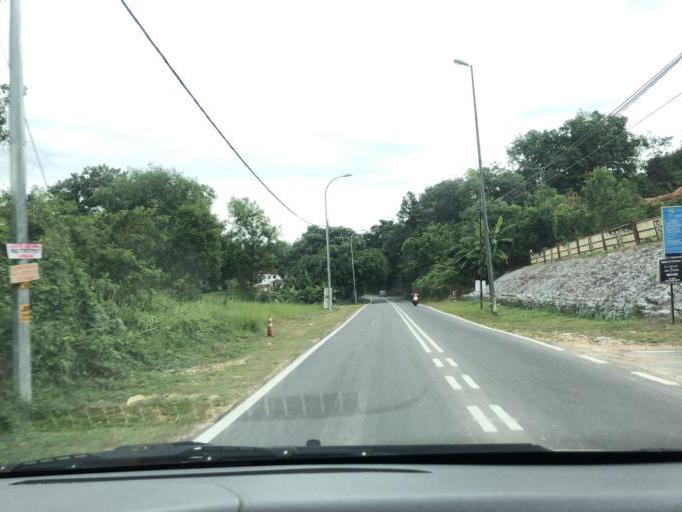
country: MY
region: Putrajaya
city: Putrajaya
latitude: 2.9192
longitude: 101.7498
